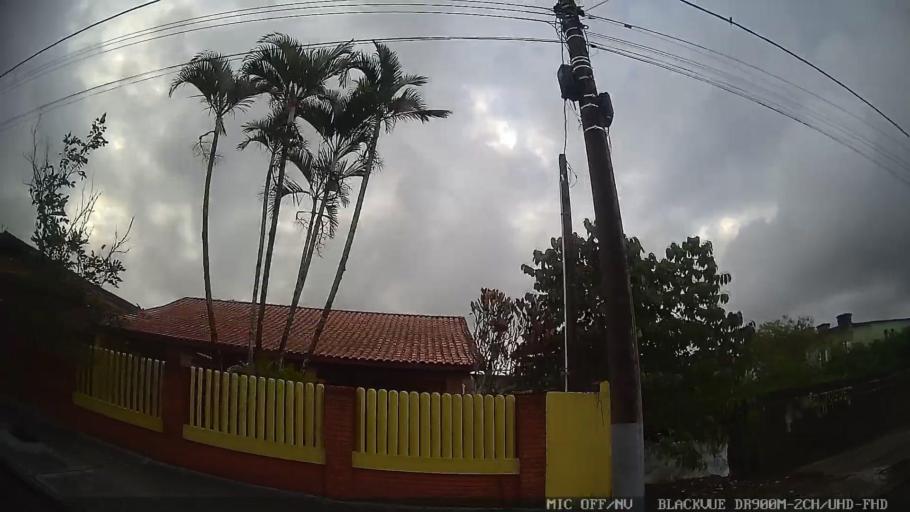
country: BR
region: Sao Paulo
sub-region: Itanhaem
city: Itanhaem
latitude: -24.2120
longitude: -46.8522
